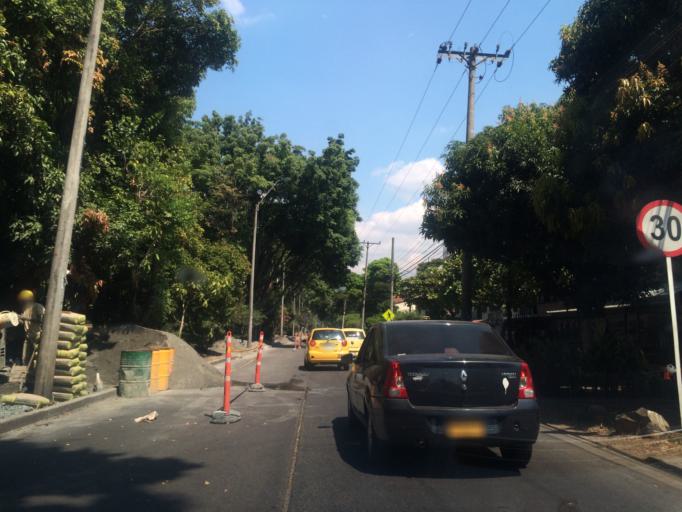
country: CO
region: Valle del Cauca
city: Cali
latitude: 3.4091
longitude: -76.5347
